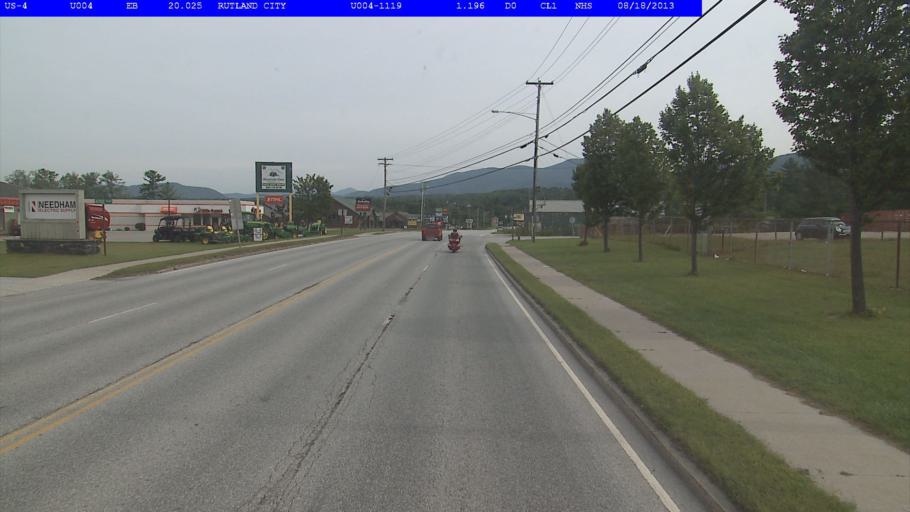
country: US
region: Vermont
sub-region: Rutland County
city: Rutland
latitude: 43.6208
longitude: -72.9539
